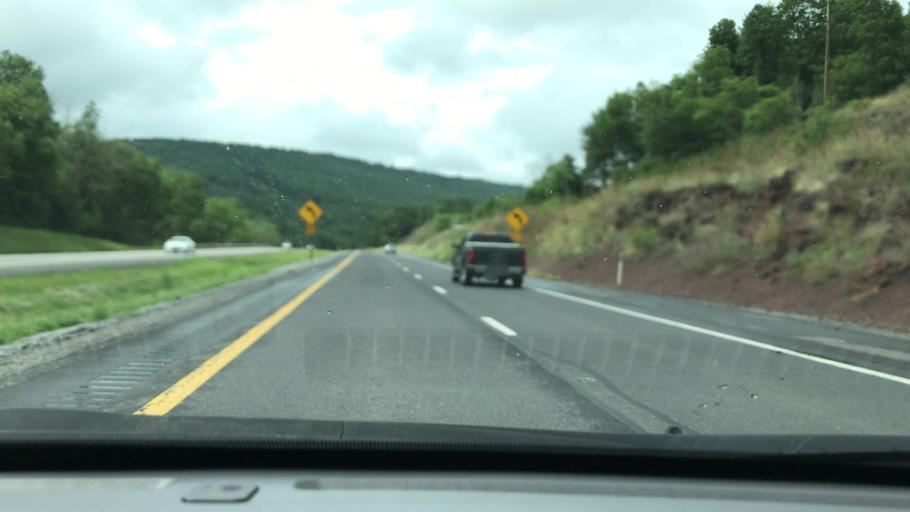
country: US
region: Pennsylvania
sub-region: Bedford County
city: Earlston
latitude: 39.9438
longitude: -78.2274
